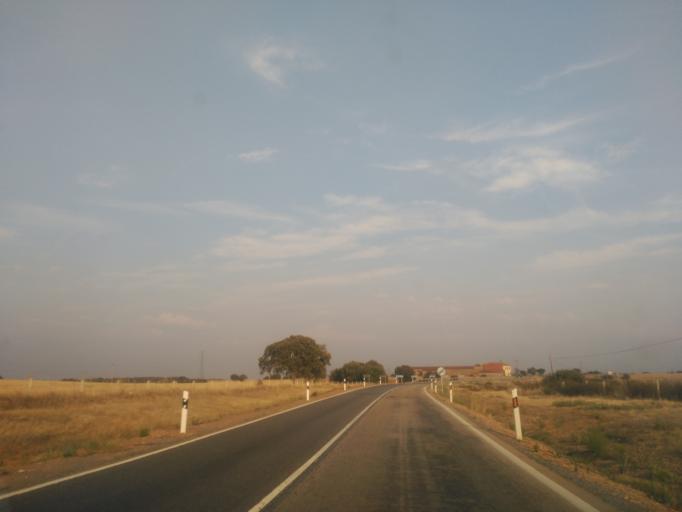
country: ES
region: Castille and Leon
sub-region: Provincia de Zamora
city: Perilla de Castro
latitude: 41.7464
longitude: -5.8413
